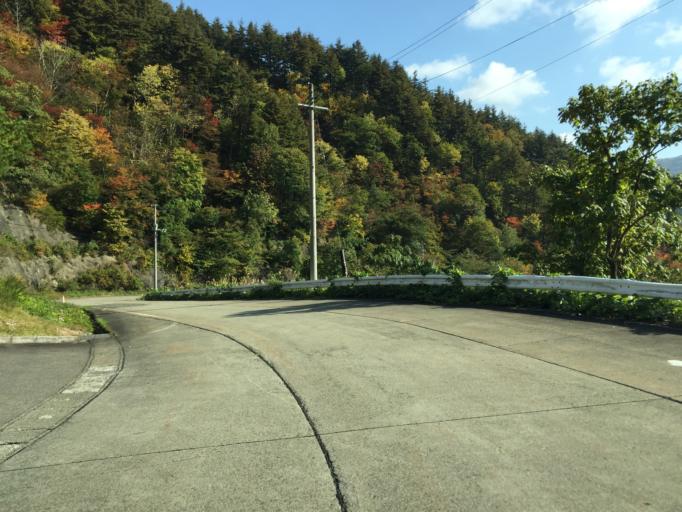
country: JP
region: Fukushima
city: Kitakata
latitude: 37.7559
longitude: 139.9029
